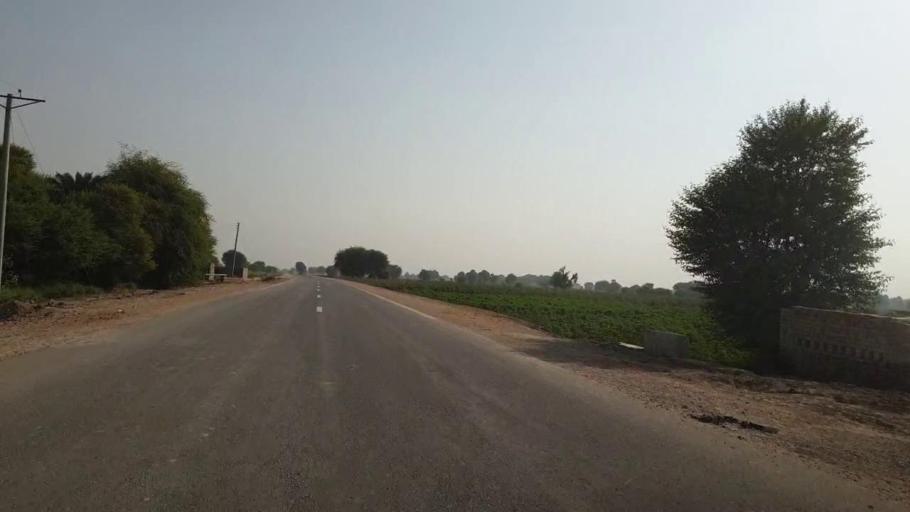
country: PK
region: Sindh
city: Bhan
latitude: 26.5321
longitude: 67.7887
